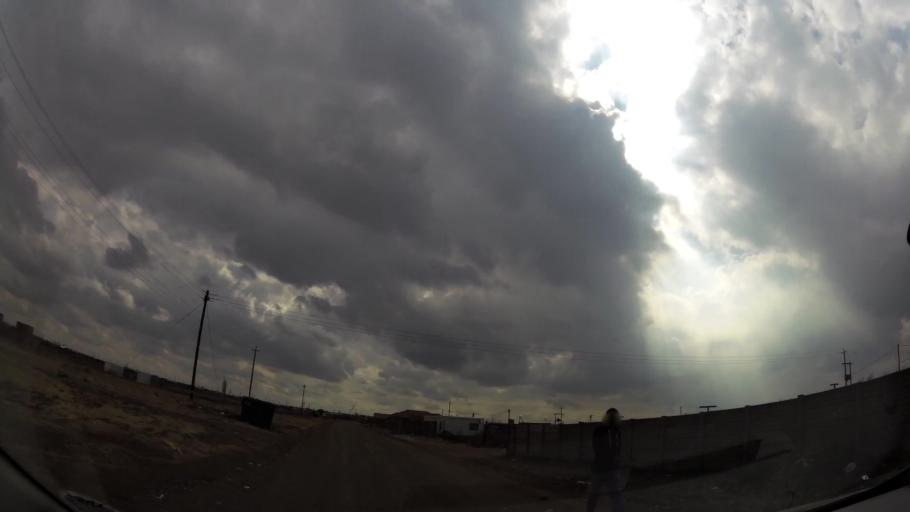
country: ZA
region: Orange Free State
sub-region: Fezile Dabi District Municipality
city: Sasolburg
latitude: -26.8545
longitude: 27.8984
